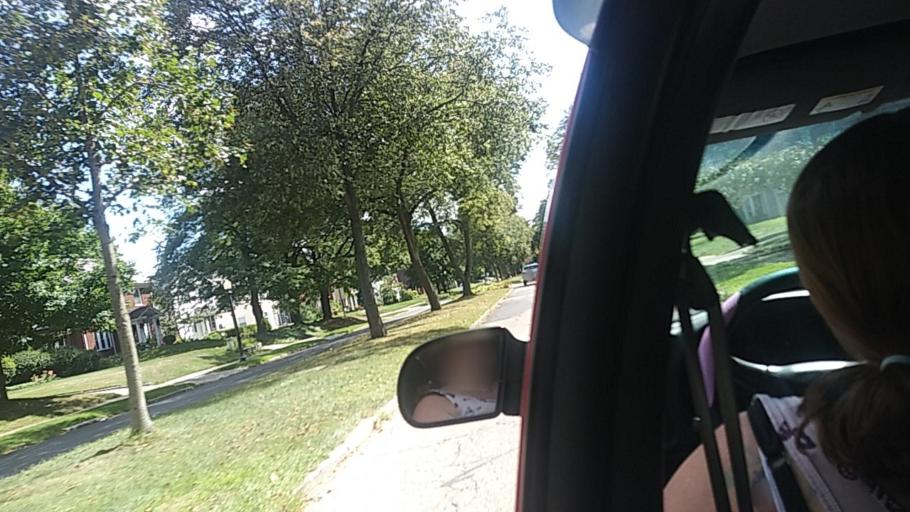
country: US
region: Ohio
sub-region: Summit County
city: Akron
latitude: 41.1082
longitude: -81.5615
